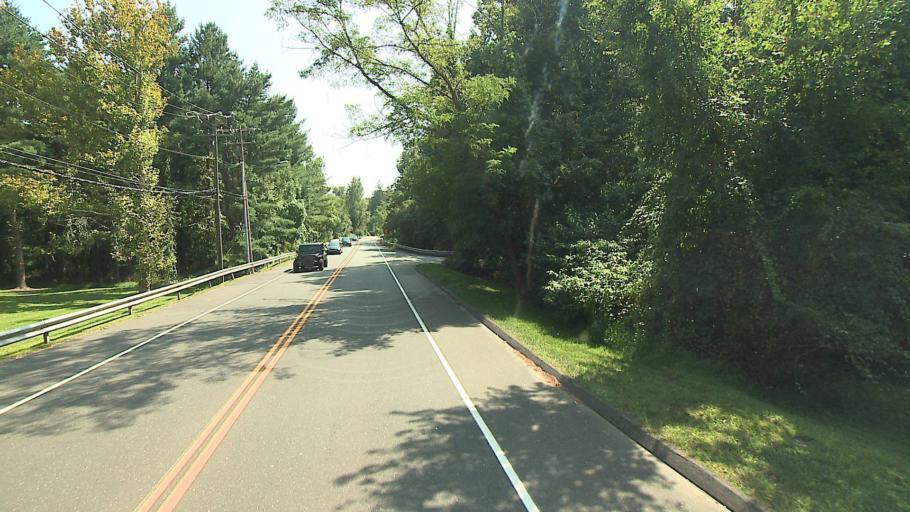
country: US
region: Connecticut
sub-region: Fairfield County
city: Westport
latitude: 41.1764
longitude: -73.3626
